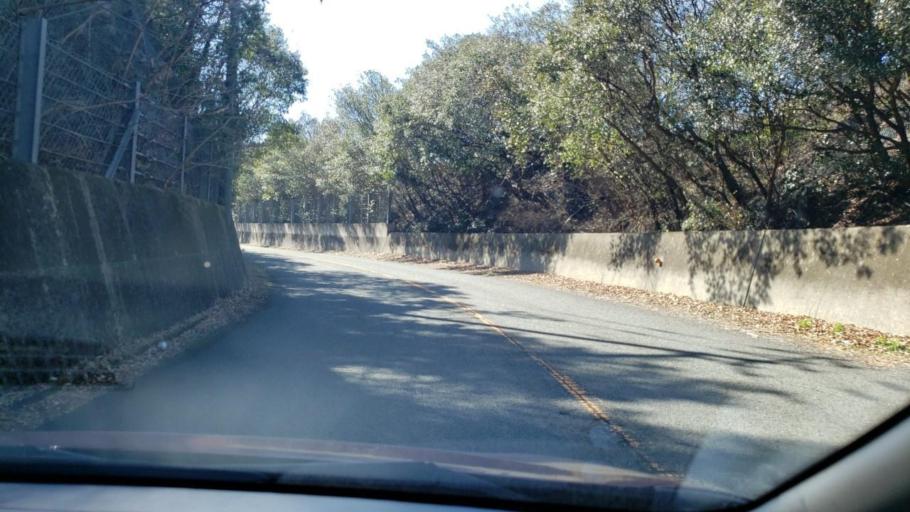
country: JP
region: Tokushima
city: Narutocho-mitsuishi
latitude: 34.2345
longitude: 134.6043
